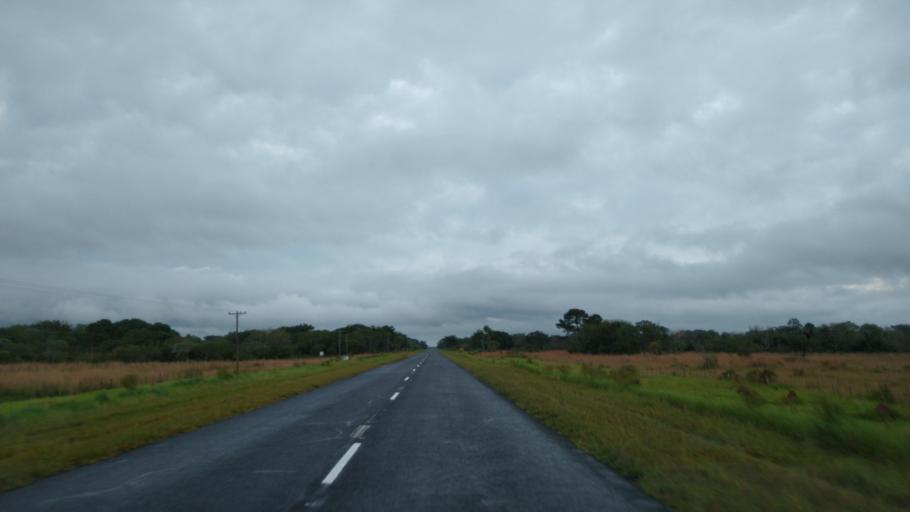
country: AR
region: Corrientes
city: Loreto
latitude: -27.7428
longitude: -57.2502
